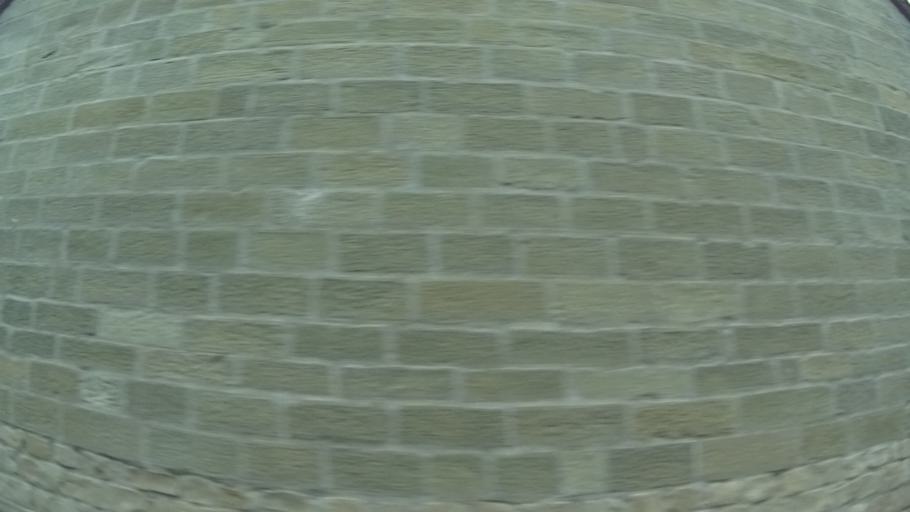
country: DE
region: Bavaria
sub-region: Regierungsbezirk Unterfranken
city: Dingolshausen
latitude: 49.9067
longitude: 10.3876
